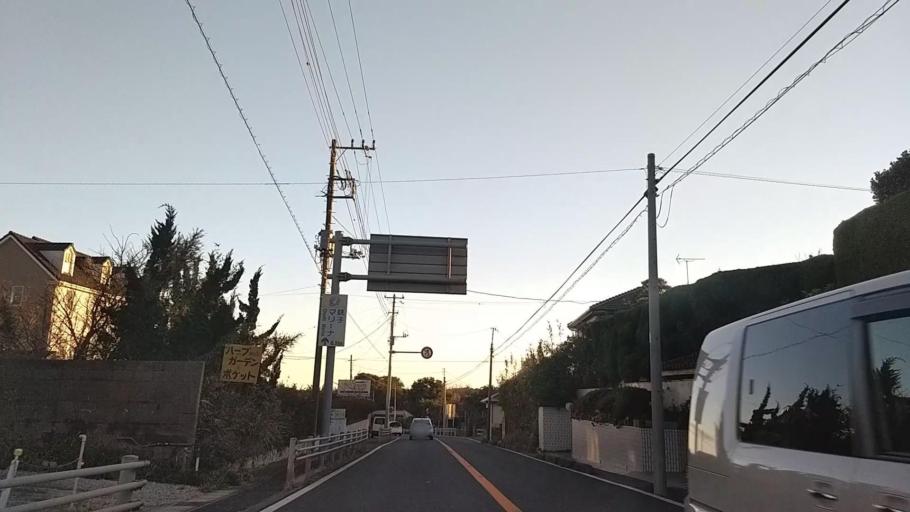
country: JP
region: Chiba
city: Hasaki
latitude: 35.7294
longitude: 140.8654
